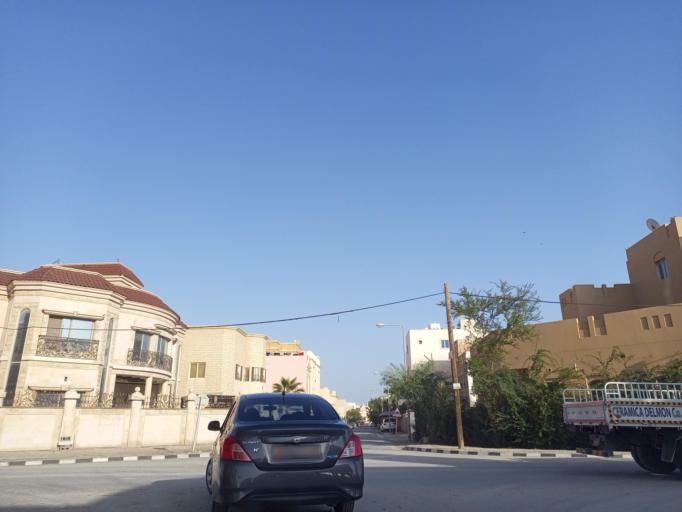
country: BH
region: Muharraq
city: Al Hadd
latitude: 26.2314
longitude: 50.6480
